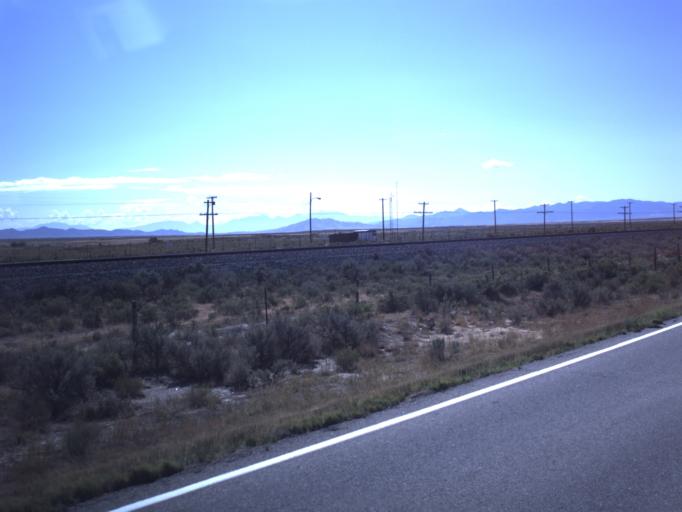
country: US
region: Utah
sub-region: Tooele County
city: Tooele
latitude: 40.2911
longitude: -112.4007
